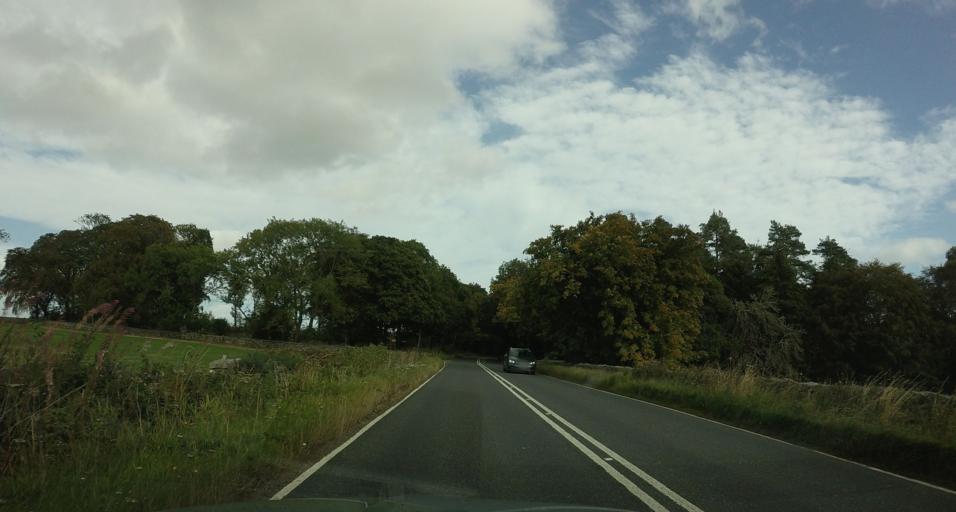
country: GB
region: Scotland
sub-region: Aberdeenshire
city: Kintore
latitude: 57.1644
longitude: -2.3677
